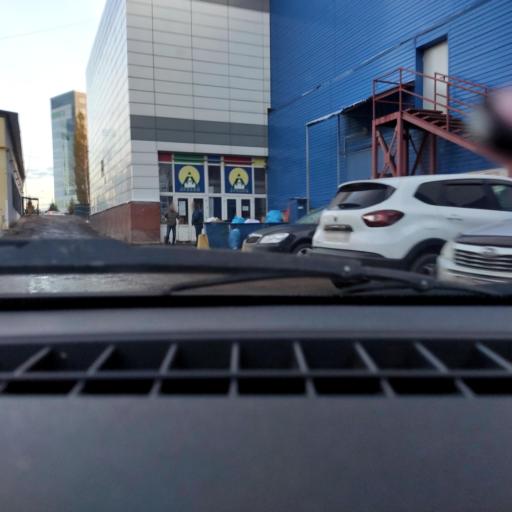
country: RU
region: Bashkortostan
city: Ufa
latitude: 54.7518
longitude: 56.0301
